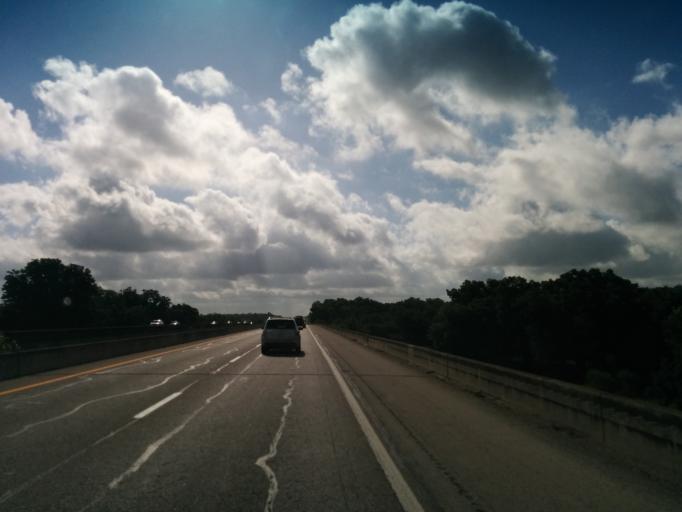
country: US
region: Texas
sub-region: Caldwell County
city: Luling
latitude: 29.6493
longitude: -97.6359
